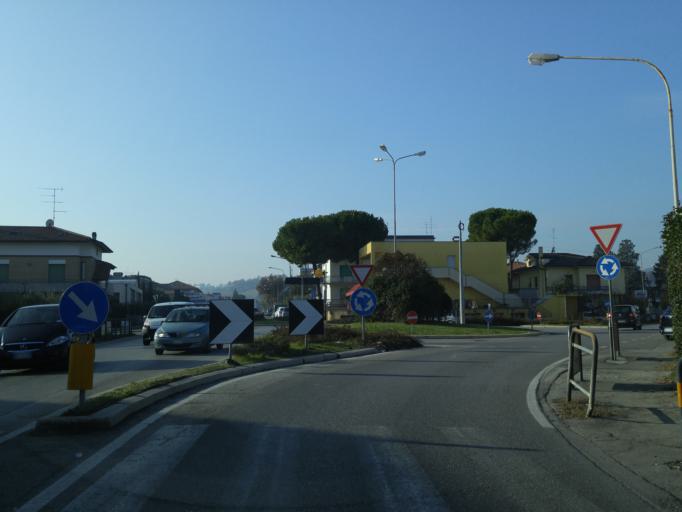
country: IT
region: The Marches
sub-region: Provincia di Pesaro e Urbino
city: Centinarola
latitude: 43.8320
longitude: 13.0009
